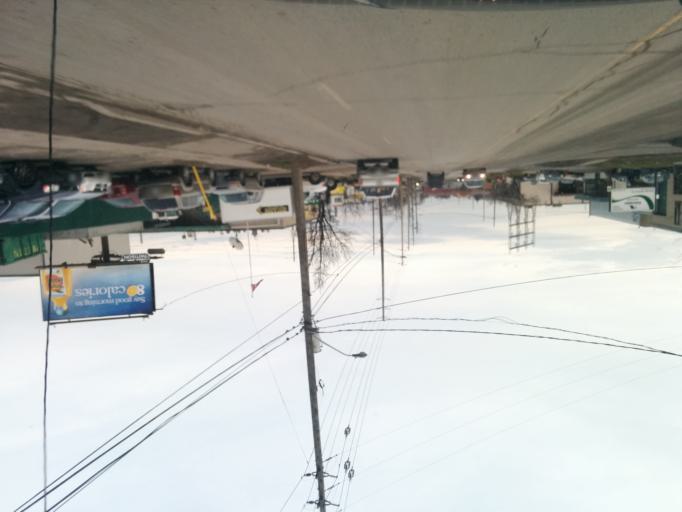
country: CA
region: Ontario
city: Etobicoke
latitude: 43.6267
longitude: -79.5424
